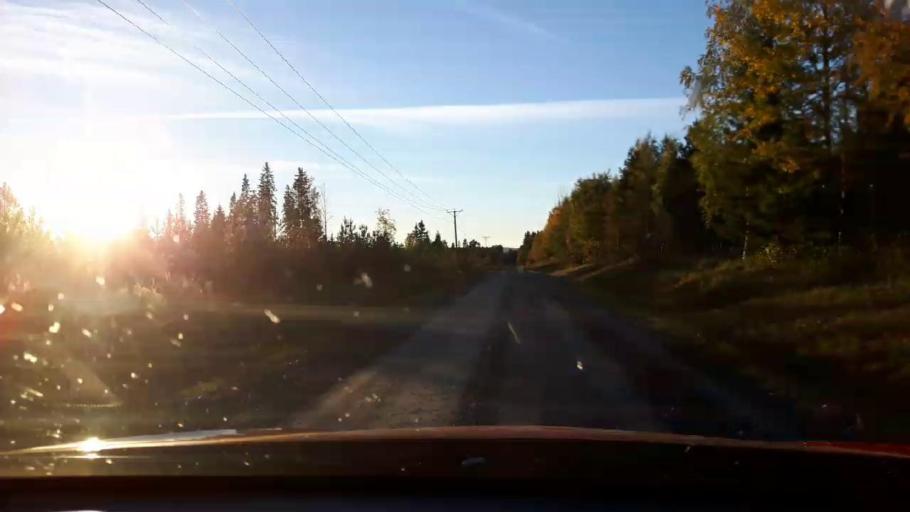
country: SE
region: Jaemtland
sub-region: Krokoms Kommun
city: Krokom
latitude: 63.4295
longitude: 14.4442
